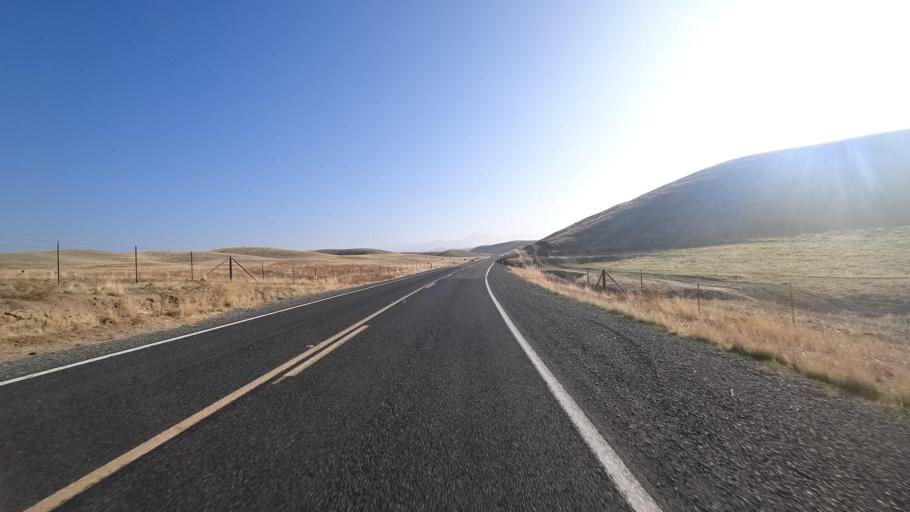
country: US
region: California
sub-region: Tulare County
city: Richgrove
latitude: 35.7438
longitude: -118.9443
